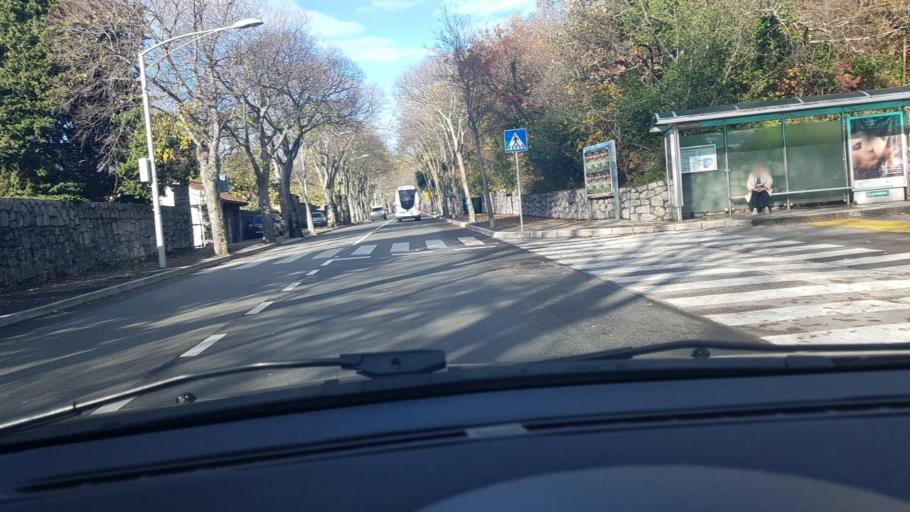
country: HR
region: Primorsko-Goranska
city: Rubesi
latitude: 45.3445
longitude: 14.3585
